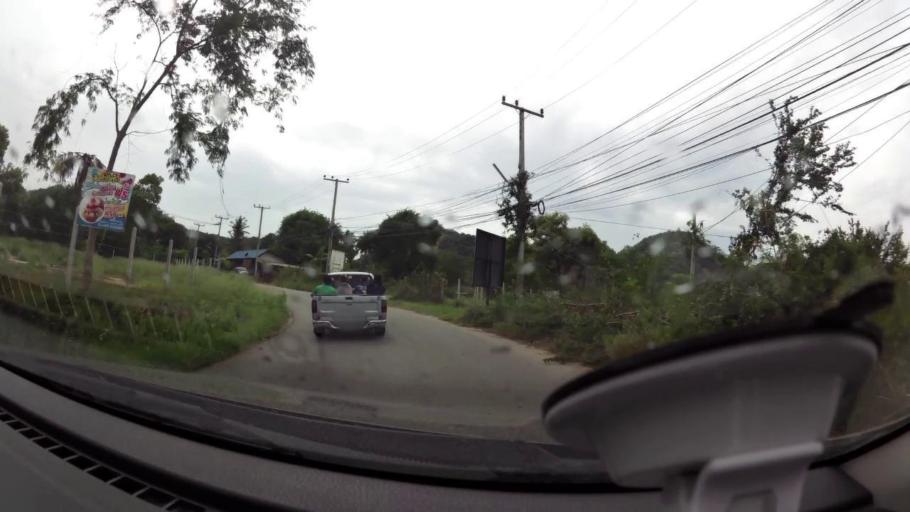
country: TH
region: Prachuap Khiri Khan
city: Pran Buri
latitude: 12.4347
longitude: 99.9763
